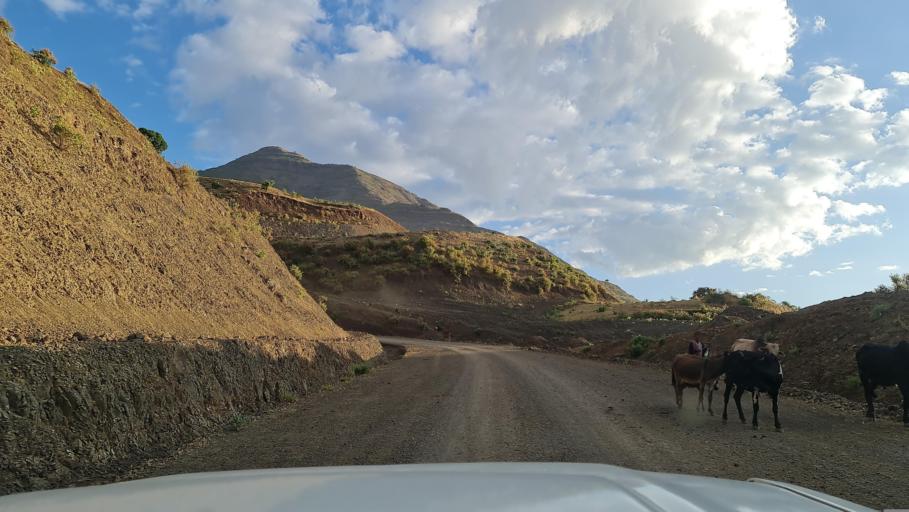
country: ET
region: Amhara
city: Debark'
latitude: 13.0276
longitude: 38.0525
